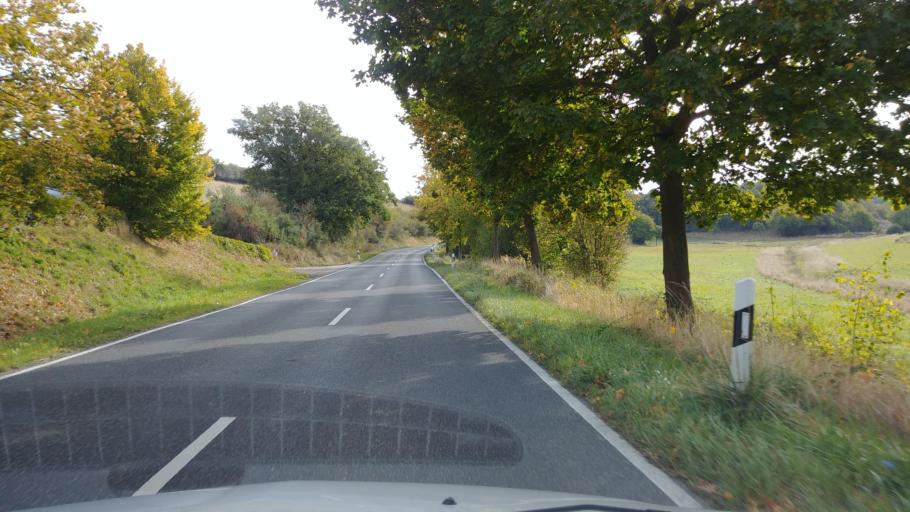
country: DE
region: Hesse
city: Taunusstein
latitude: 50.1893
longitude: 8.1290
